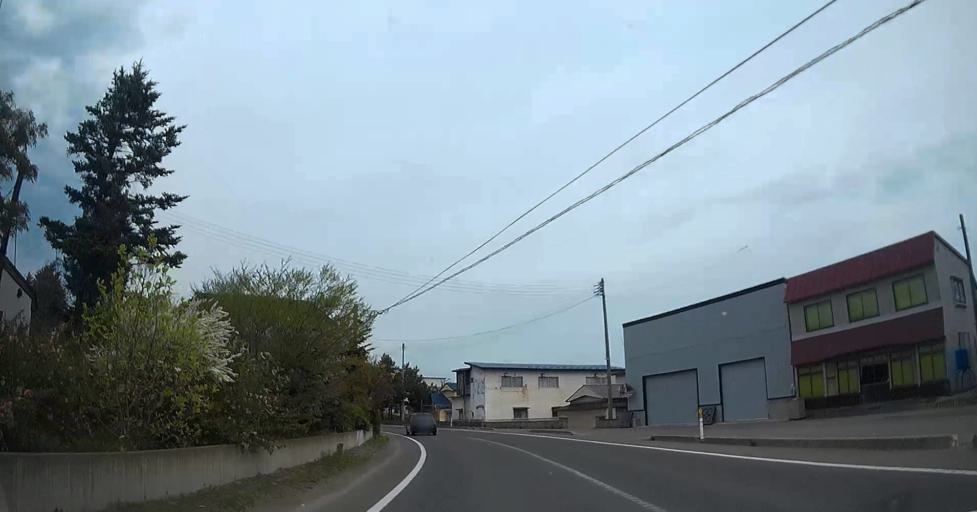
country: JP
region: Aomori
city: Shimokizukuri
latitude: 40.9706
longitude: 140.3677
